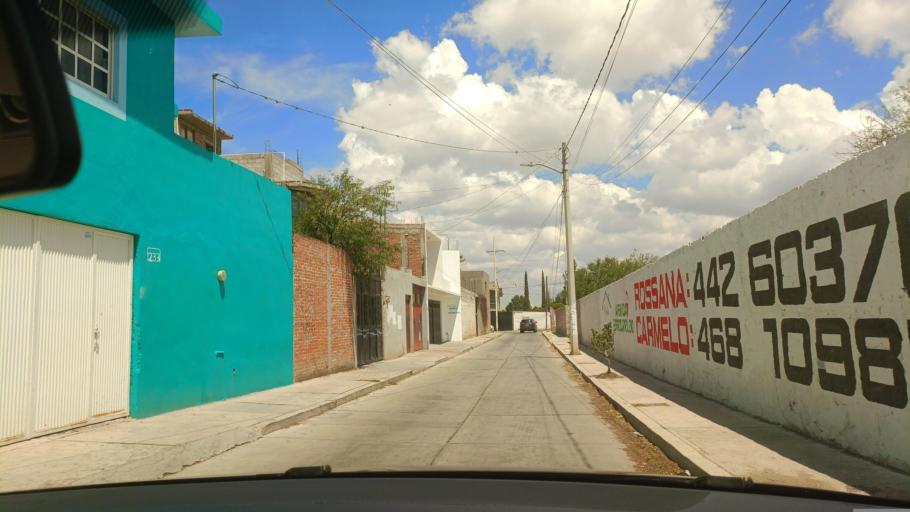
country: MX
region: Guanajuato
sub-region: San Luis de la Paz
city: San Luis de la Paz
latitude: 21.3032
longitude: -100.5188
